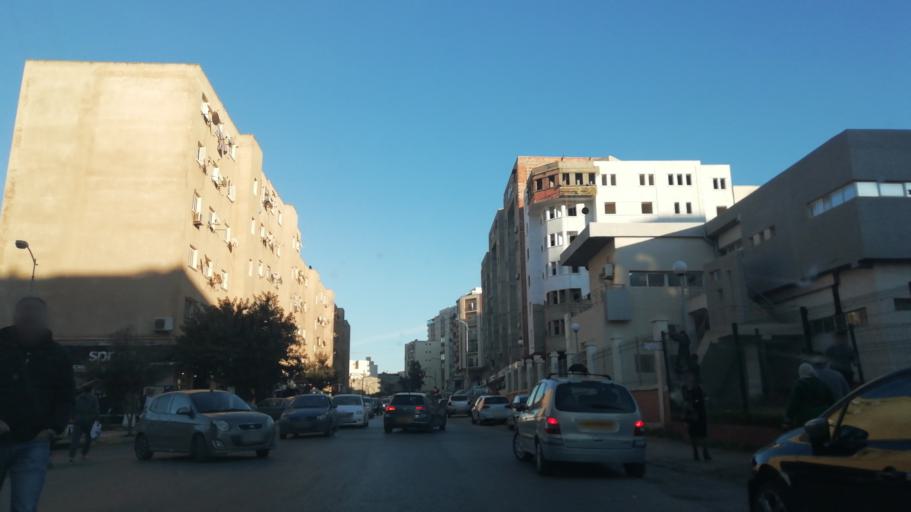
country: DZ
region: Oran
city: Bir el Djir
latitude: 35.7230
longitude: -0.5893
